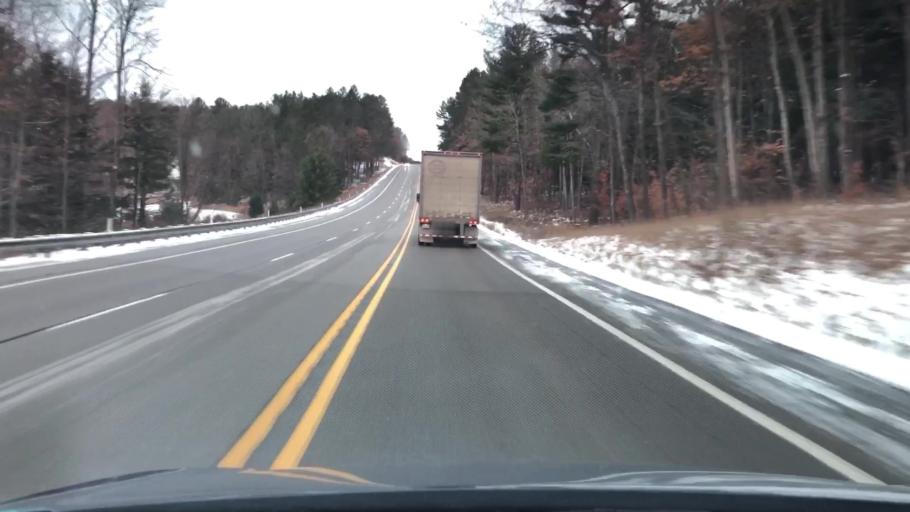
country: US
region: Michigan
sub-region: Wexford County
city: Cadillac
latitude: 44.1843
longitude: -85.3860
